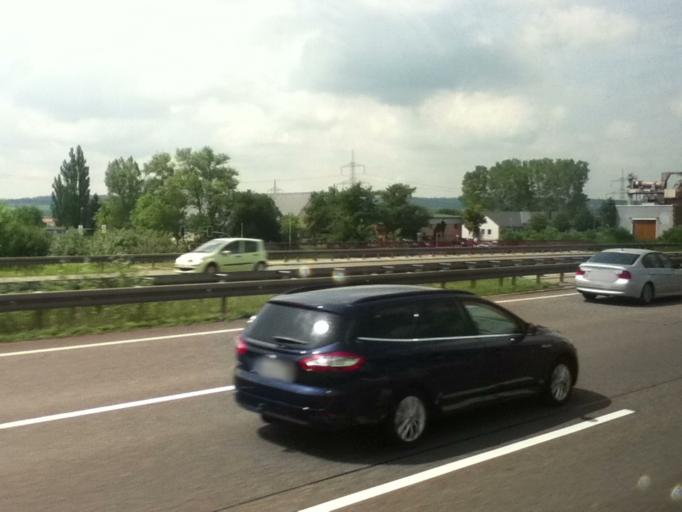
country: DE
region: Thuringia
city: Hetschburg
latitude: 50.9442
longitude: 11.2978
